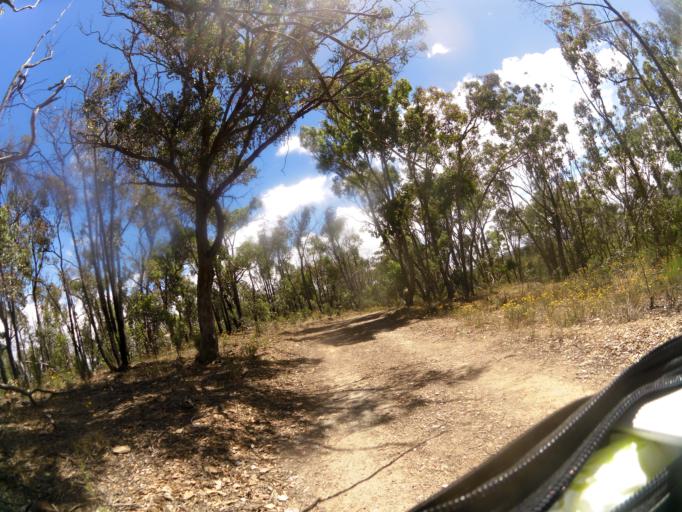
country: AU
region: Victoria
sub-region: Mount Alexander
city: Castlemaine
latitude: -37.0682
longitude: 144.2651
